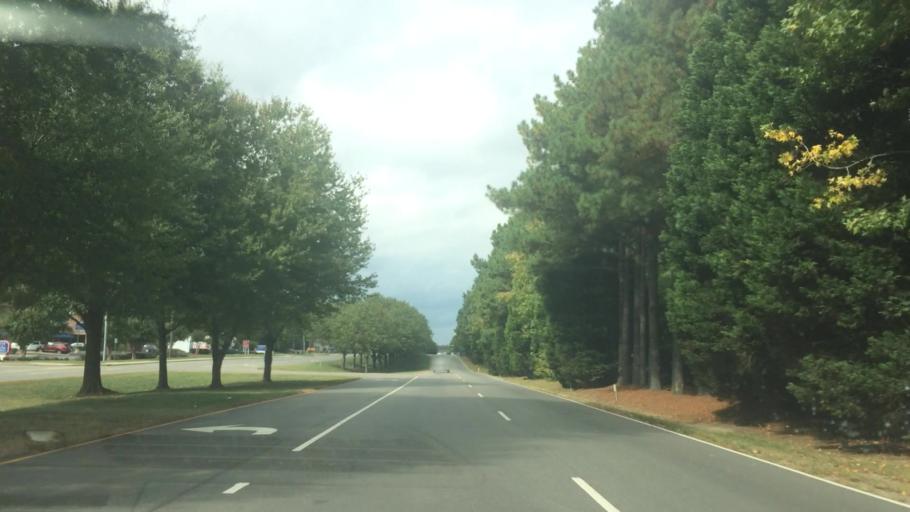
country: US
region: Virginia
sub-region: James City County
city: Williamsburg
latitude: 37.3076
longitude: -76.7299
